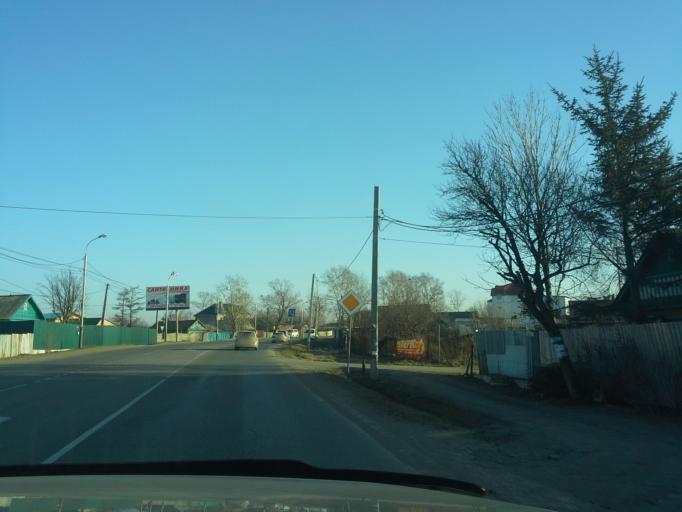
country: RU
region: Khabarovsk Krai
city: Topolevo
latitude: 48.4728
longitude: 135.1753
